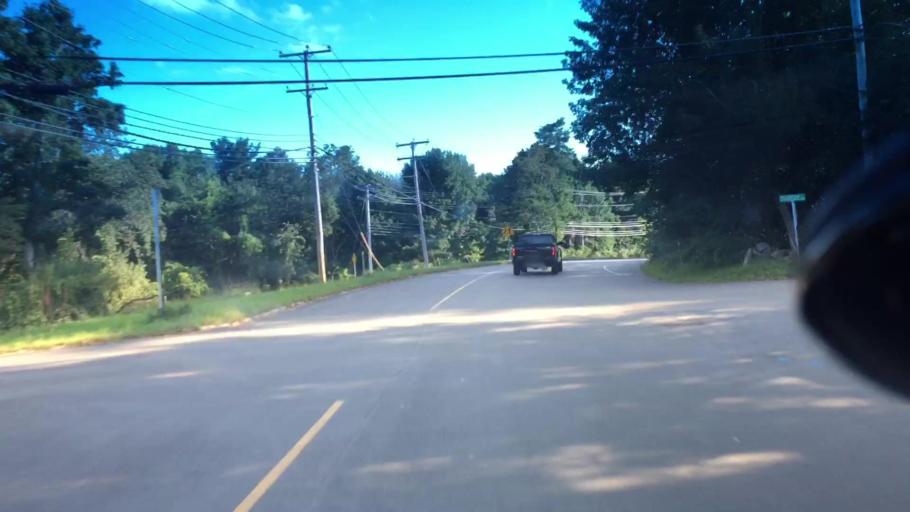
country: US
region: New Hampshire
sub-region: Rockingham County
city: Hampton
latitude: 42.9353
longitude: -70.8383
